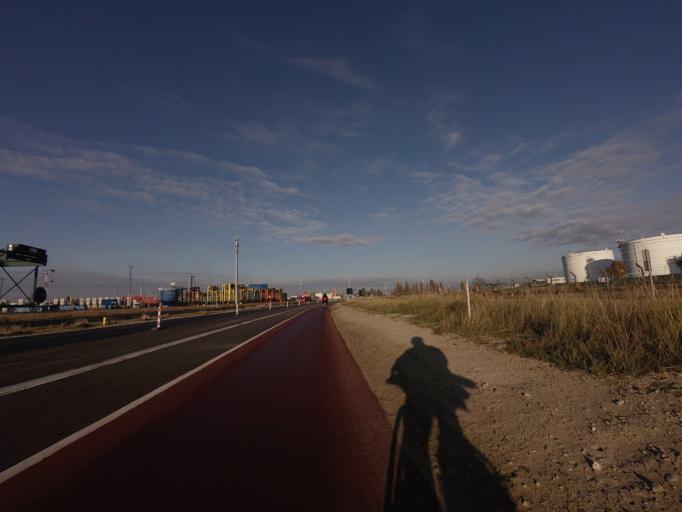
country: BE
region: Flanders
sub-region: Provincie Antwerpen
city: Stabroek
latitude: 51.3370
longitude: 4.2834
